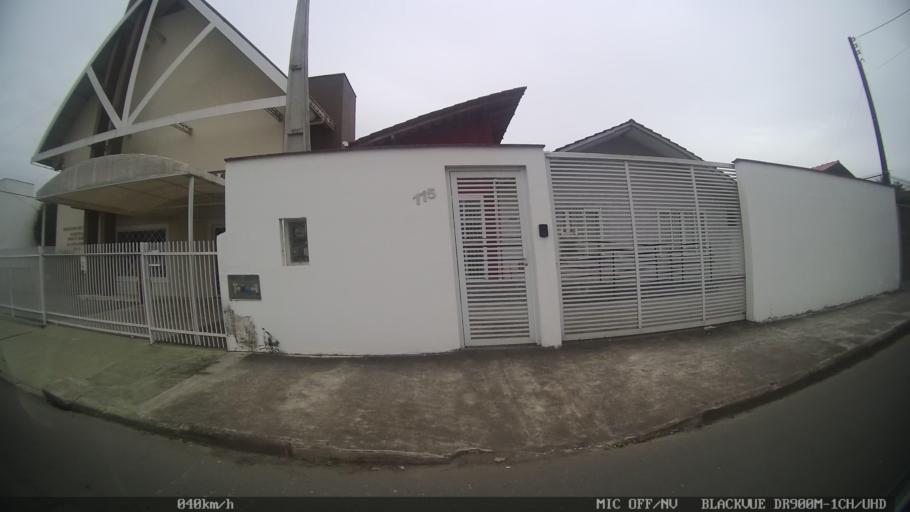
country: BR
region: Santa Catarina
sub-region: Joinville
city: Joinville
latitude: -26.2747
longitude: -48.8345
